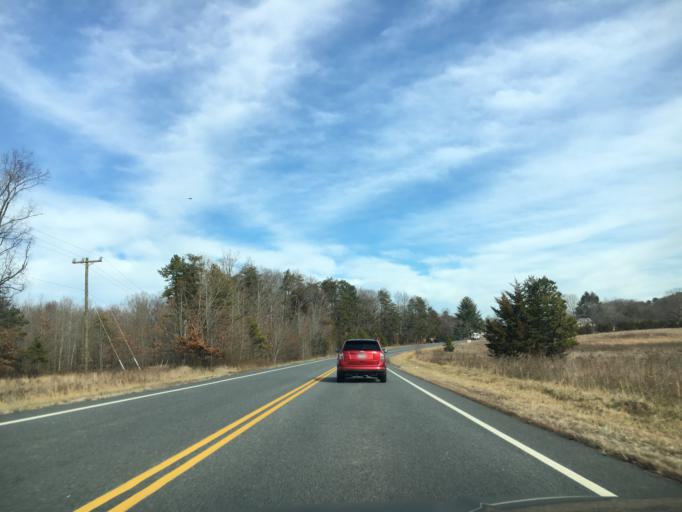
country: US
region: Virginia
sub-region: Louisa County
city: Louisa
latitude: 38.0421
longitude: -77.8860
